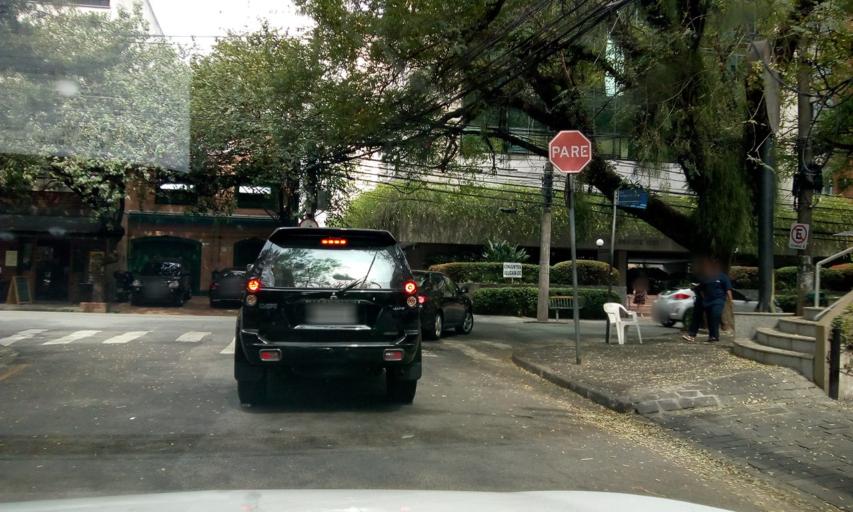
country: BR
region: Sao Paulo
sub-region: Sao Paulo
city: Sao Paulo
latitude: -23.5824
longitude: -46.6820
